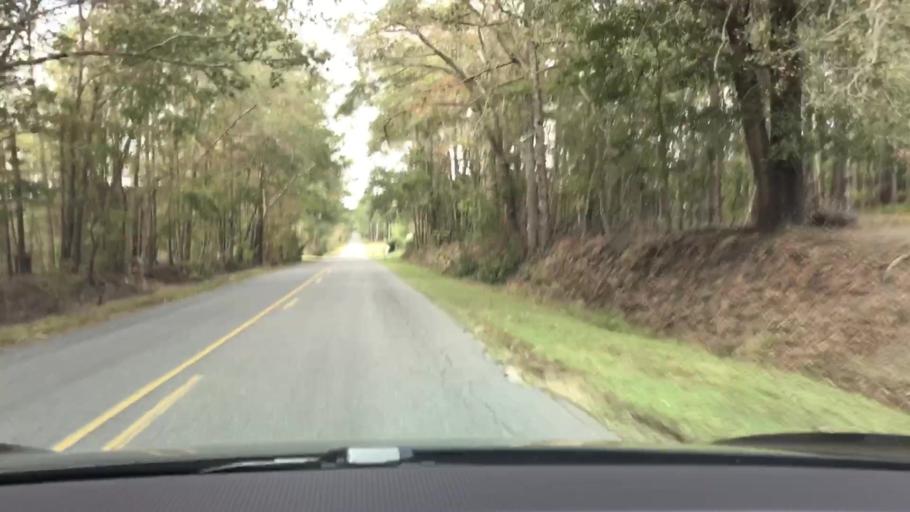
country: US
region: Georgia
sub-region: Jefferson County
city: Wadley
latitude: 32.7995
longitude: -82.3512
